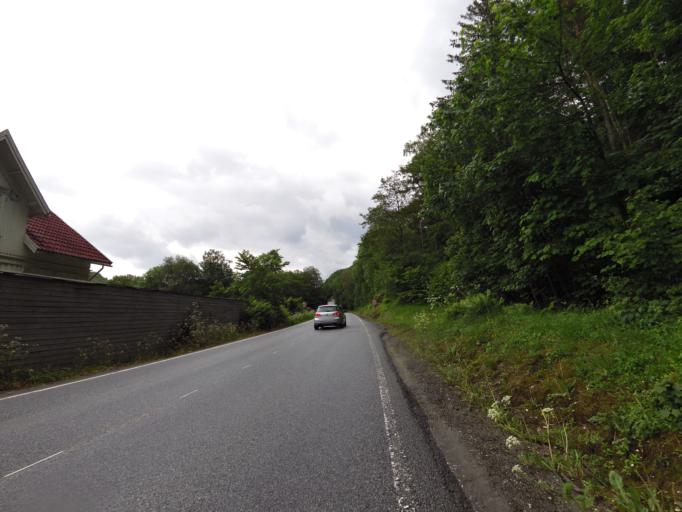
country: NO
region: Vest-Agder
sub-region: Farsund
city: Farsund
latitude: 58.1010
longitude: 6.8636
